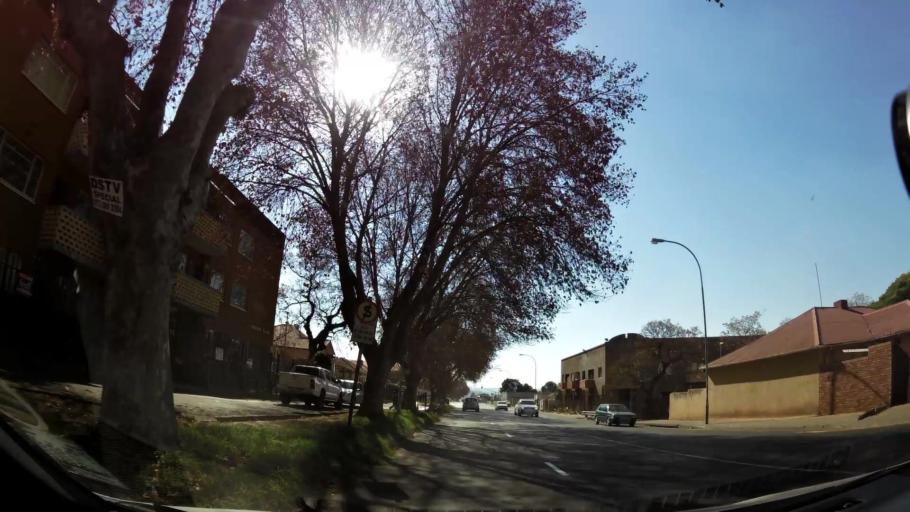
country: ZA
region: Gauteng
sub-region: City of Johannesburg Metropolitan Municipality
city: Johannesburg
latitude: -26.2528
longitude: 28.0552
